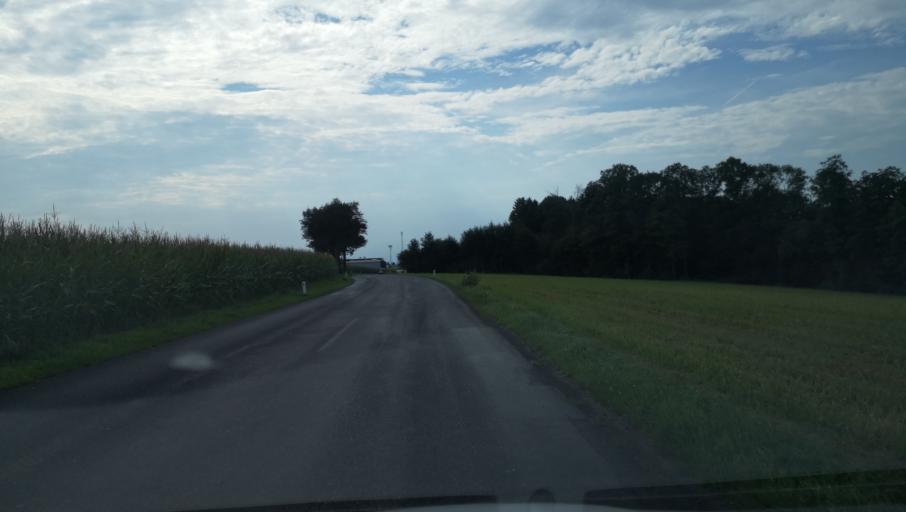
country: AT
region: Lower Austria
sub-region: Politischer Bezirk Amstetten
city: Amstetten
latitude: 48.1471
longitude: 14.8623
